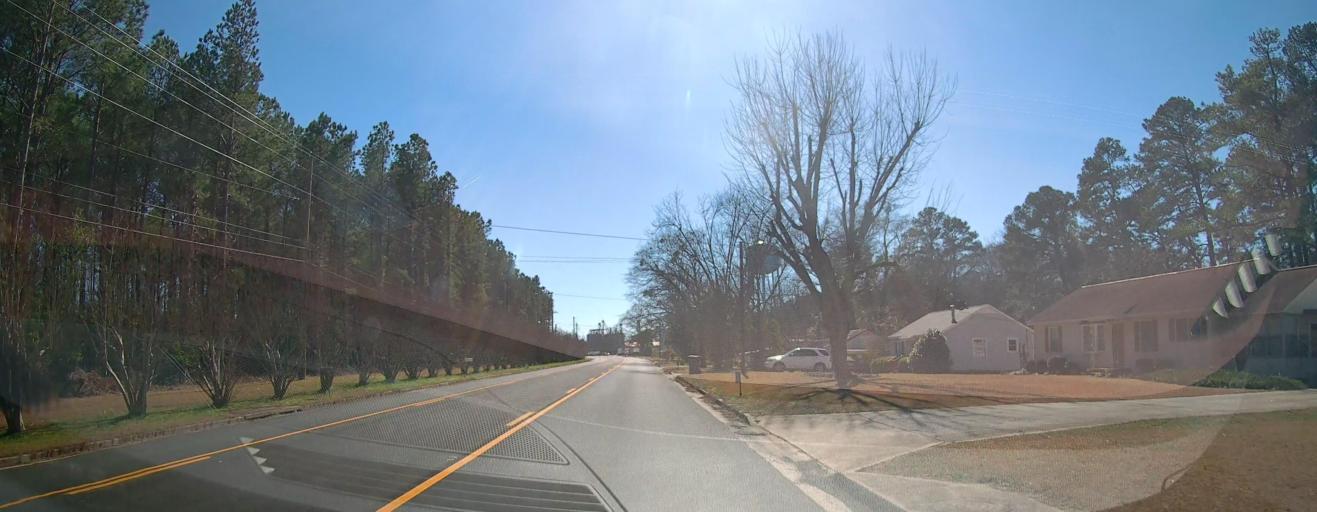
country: US
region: Georgia
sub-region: Macon County
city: Marshallville
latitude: 32.4635
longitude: -83.9390
